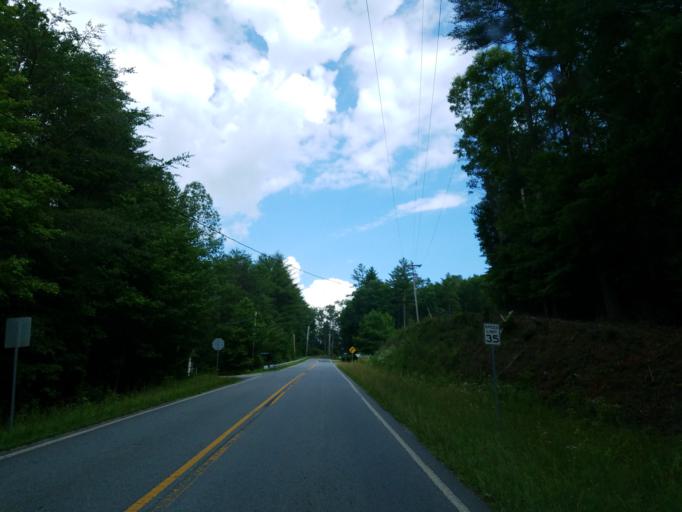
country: US
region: Georgia
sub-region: Fannin County
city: Blue Ridge
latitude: 34.7889
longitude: -84.2699
